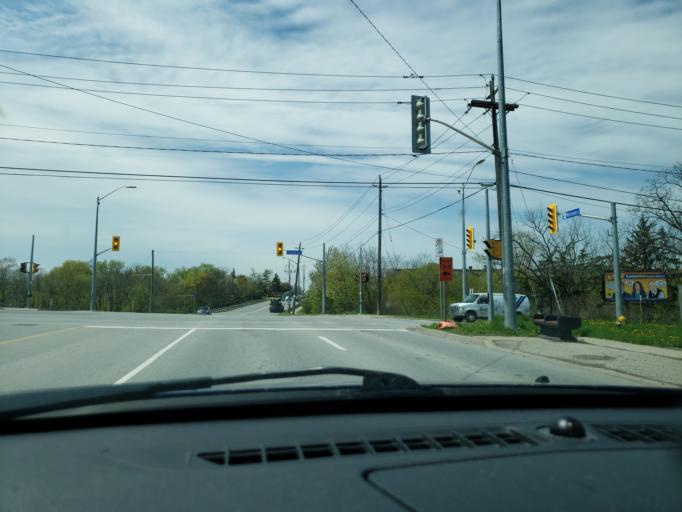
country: CA
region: Ontario
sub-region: Regional Municipality of Niagara
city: St. Catharines
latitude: 43.1585
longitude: -79.2285
